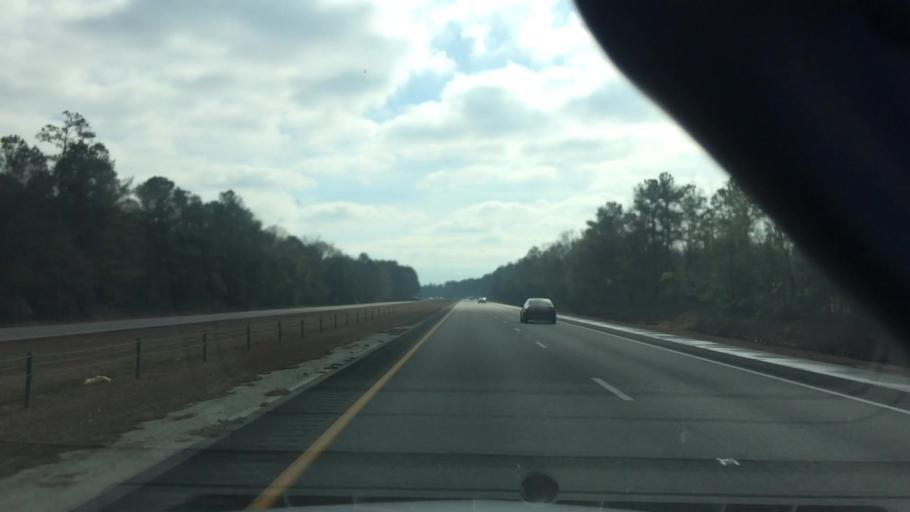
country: US
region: North Carolina
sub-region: Pender County
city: Burgaw
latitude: 34.5440
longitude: -77.8934
